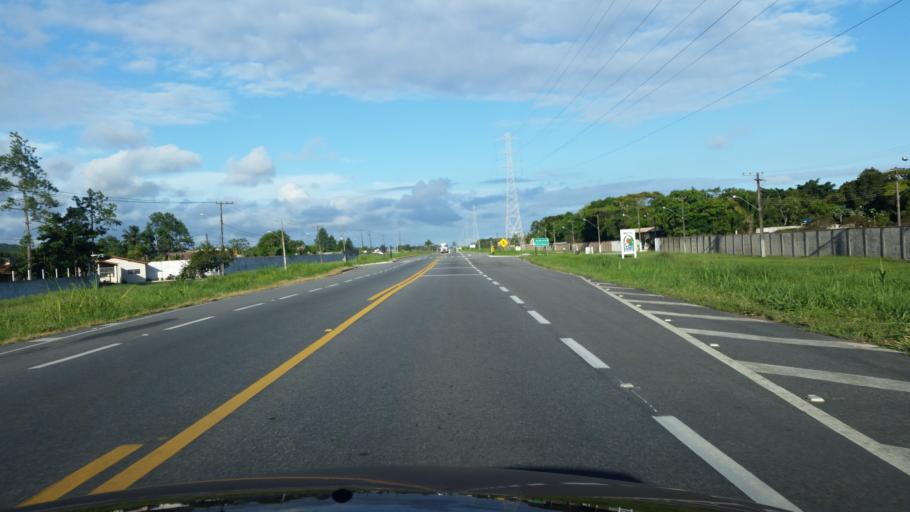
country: BR
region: Sao Paulo
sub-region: Peruibe
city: Peruibe
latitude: -24.2764
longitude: -46.9801
